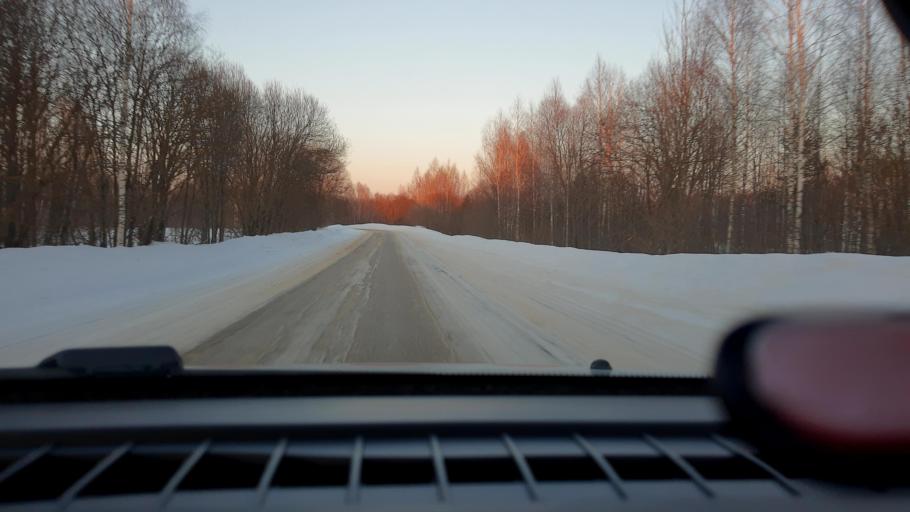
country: RU
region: Nizjnij Novgorod
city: Lyskovo
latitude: 56.1450
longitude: 45.1193
